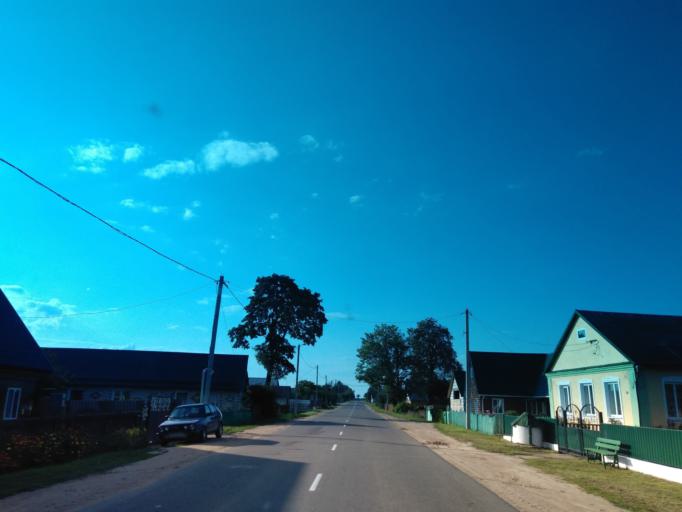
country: BY
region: Minsk
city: Kapyl'
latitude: 53.1692
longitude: 27.0804
